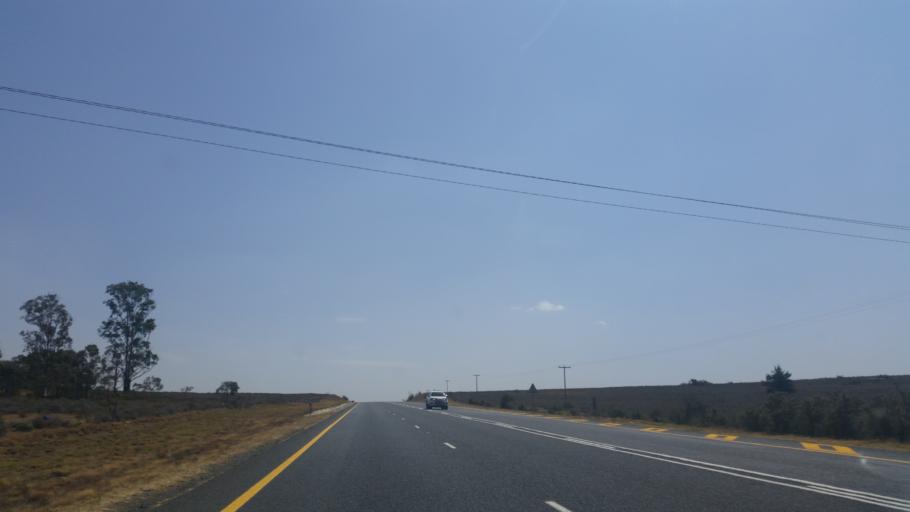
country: ZA
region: Orange Free State
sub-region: Thabo Mofutsanyana District Municipality
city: Bethlehem
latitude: -28.3046
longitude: 28.5713
